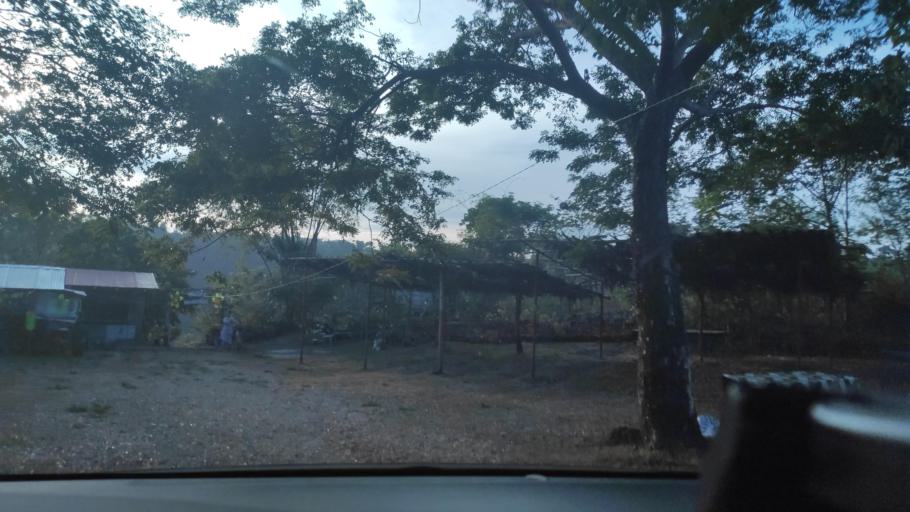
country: PH
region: Ilocos
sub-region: Province of Pangasinan
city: Balingasay
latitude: 16.3083
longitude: 119.8688
